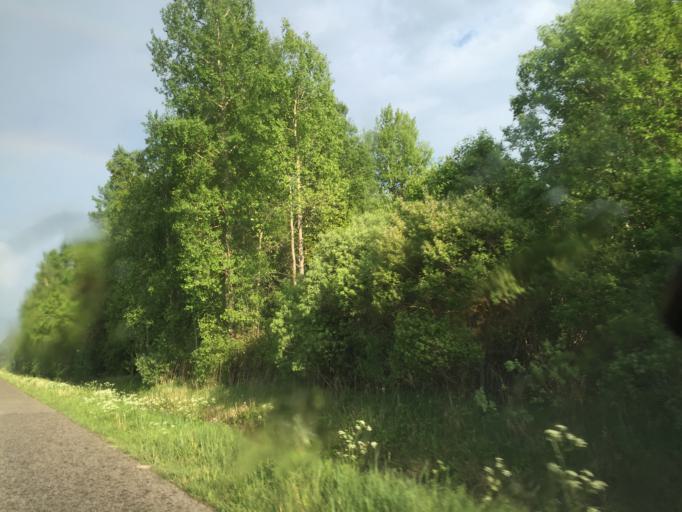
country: LT
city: Salantai
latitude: 56.0626
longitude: 21.4429
